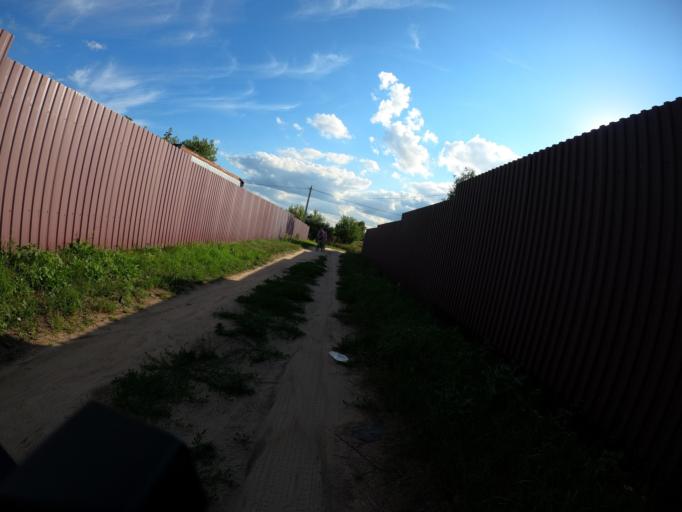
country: RU
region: Moskovskaya
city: Ramenskoye
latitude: 55.5407
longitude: 38.2926
